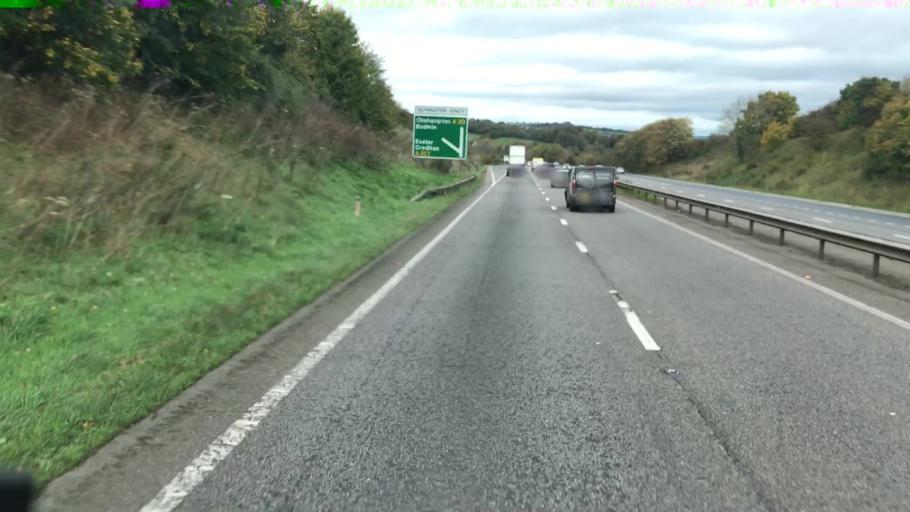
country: GB
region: England
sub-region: Devon
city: Exeter
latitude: 50.6962
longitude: -3.5411
